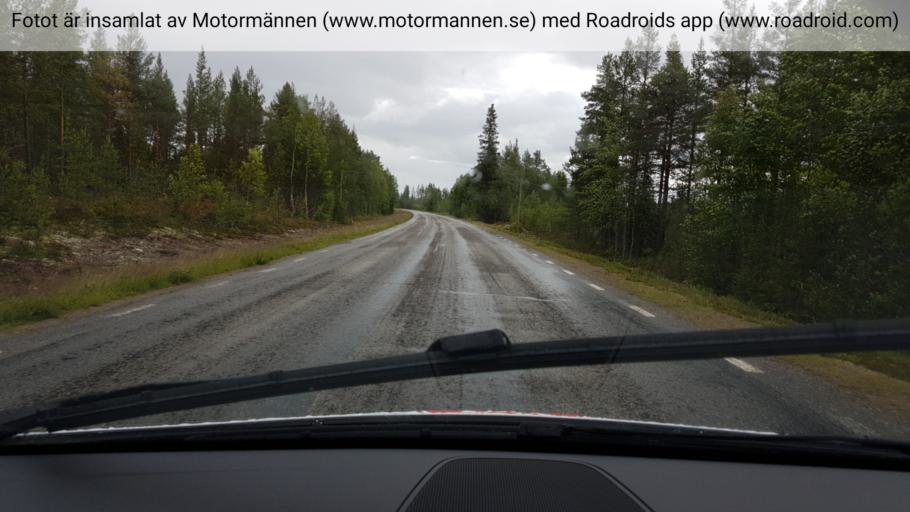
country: SE
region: Jaemtland
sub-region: Harjedalens Kommun
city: Sveg
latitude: 62.4362
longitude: 13.8794
